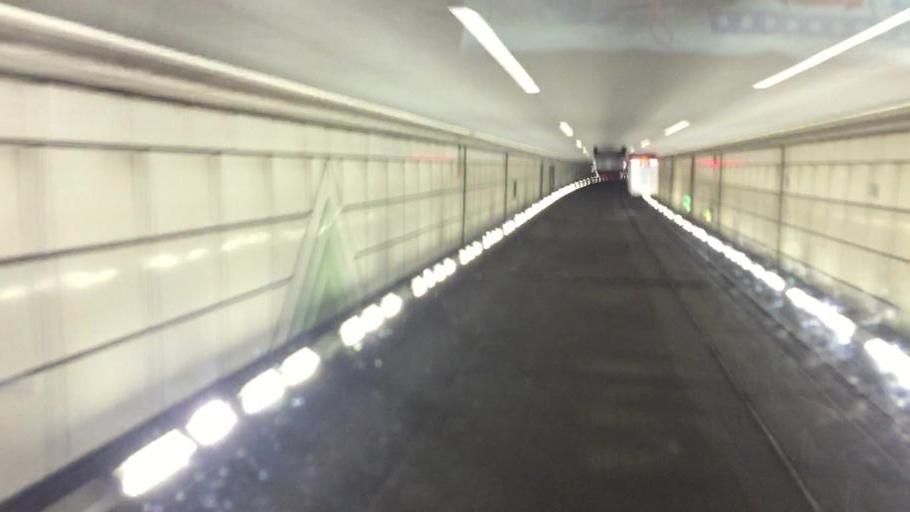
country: JP
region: Kanagawa
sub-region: Kawasaki-shi
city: Kawasaki
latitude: 35.5032
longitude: 139.7696
